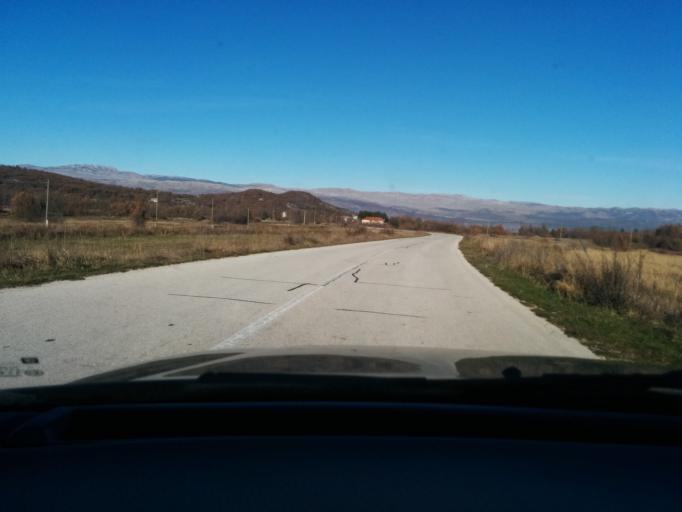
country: HR
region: Splitsko-Dalmatinska
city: Hrvace
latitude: 43.7450
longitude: 16.5462
